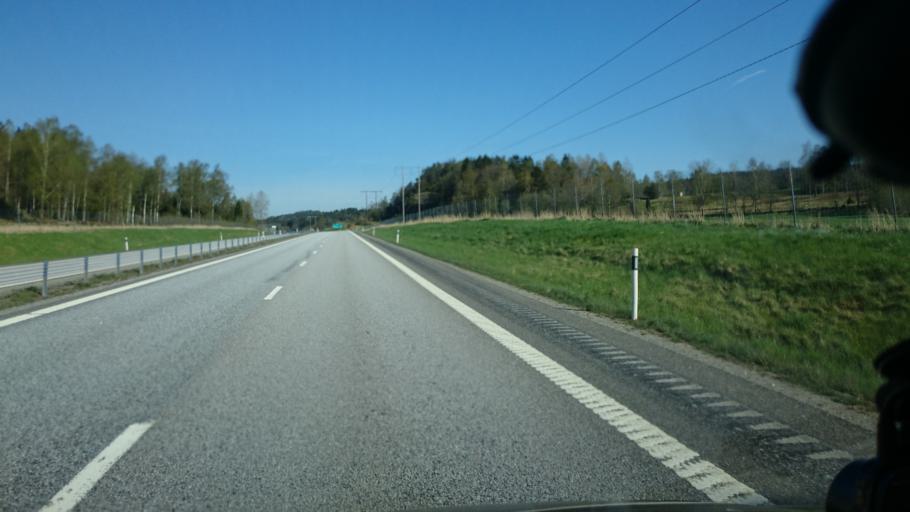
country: SE
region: Vaestra Goetaland
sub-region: Munkedals Kommun
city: Munkedal
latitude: 58.5232
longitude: 11.5469
